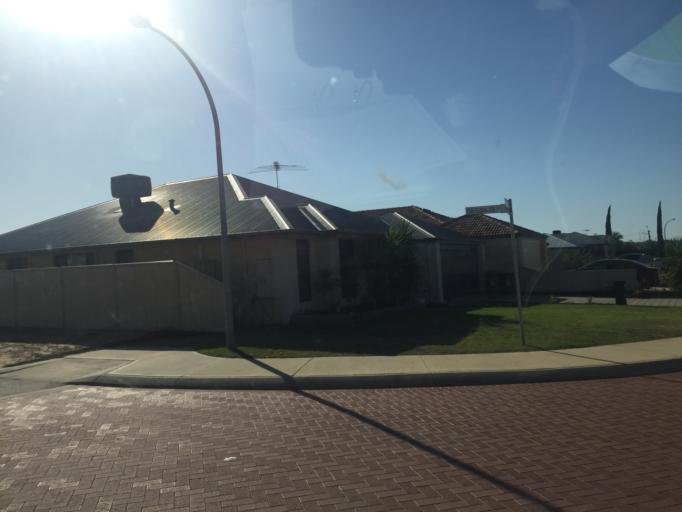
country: AU
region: Western Australia
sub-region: Canning
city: East Cannington
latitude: -32.0028
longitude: 115.9806
